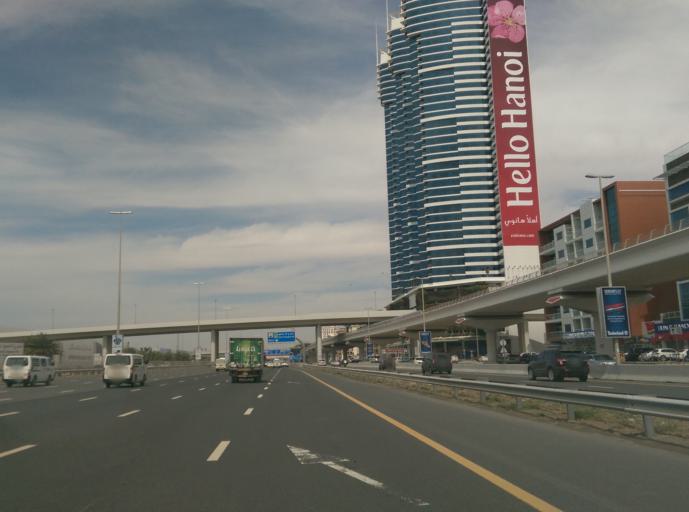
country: AE
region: Dubai
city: Dubai
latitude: 25.1116
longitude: 55.1862
